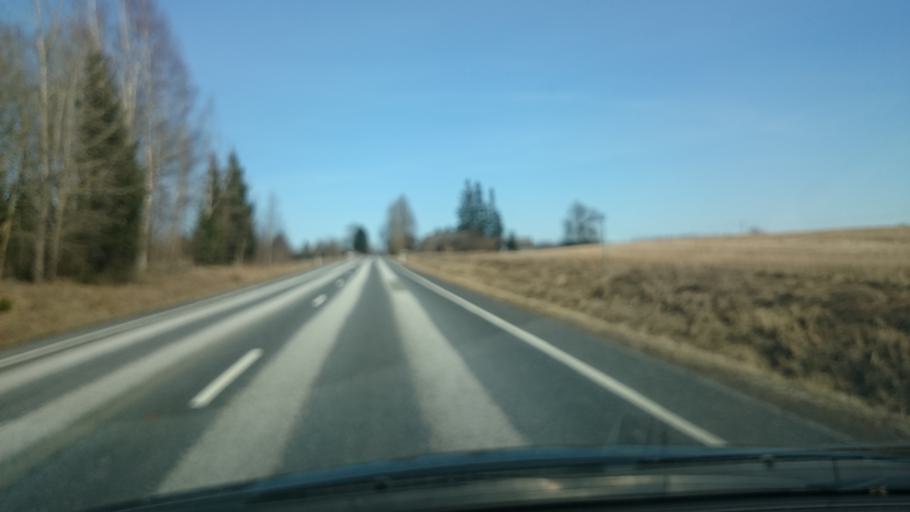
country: EE
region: Jaervamaa
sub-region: Tueri vald
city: Sarevere
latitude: 58.7480
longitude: 25.3156
